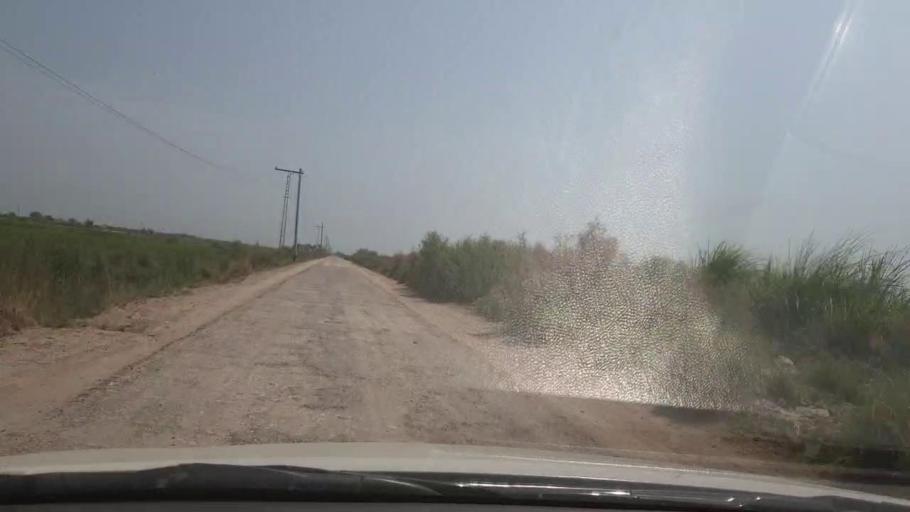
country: PK
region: Sindh
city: Garhi Yasin
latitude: 27.9655
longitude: 68.5043
